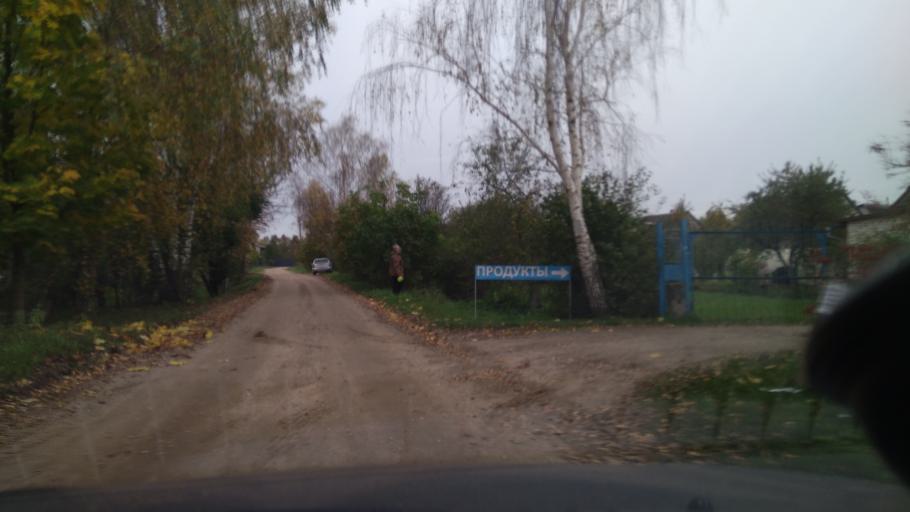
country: BY
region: Minsk
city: Rudzyensk
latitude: 53.6073
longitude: 27.8483
